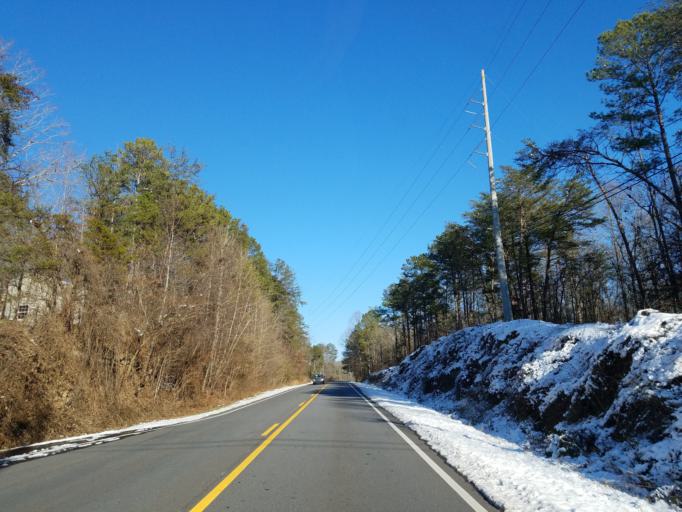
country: US
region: Georgia
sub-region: Dawson County
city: Dawsonville
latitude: 34.3528
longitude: -84.0986
